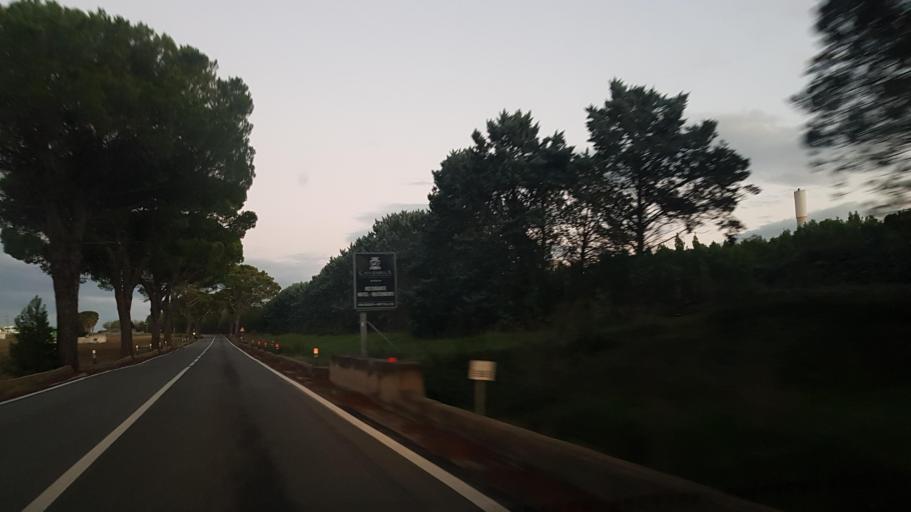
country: IT
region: Basilicate
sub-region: Provincia di Matera
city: Matera
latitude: 40.6790
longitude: 16.6507
